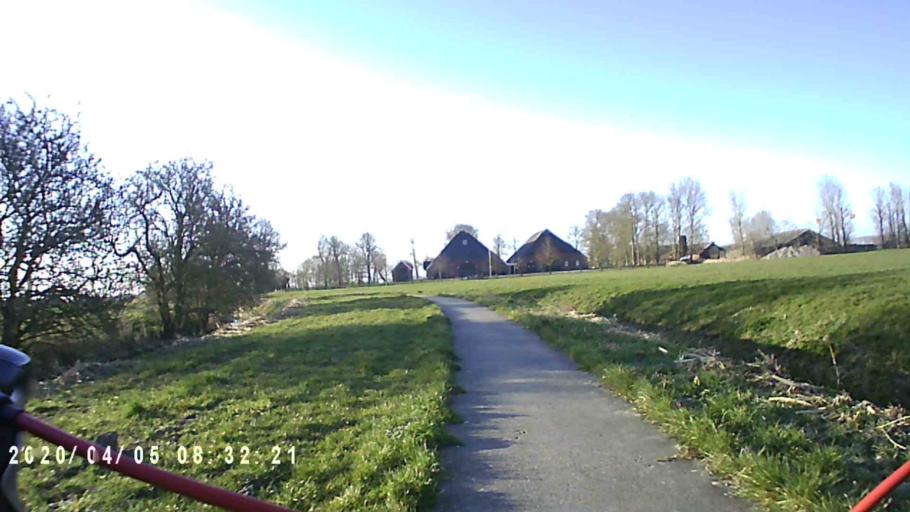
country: NL
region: Groningen
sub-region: Gemeente Winsum
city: Winsum
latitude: 53.3265
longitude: 6.4854
